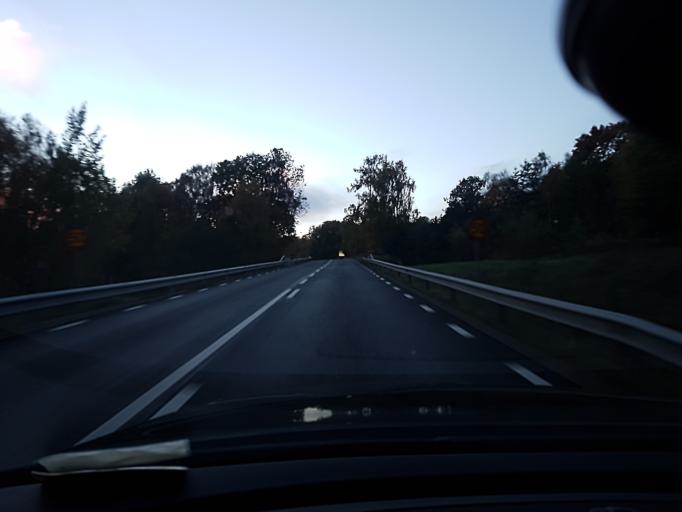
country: SE
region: Halland
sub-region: Laholms Kommun
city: Veinge
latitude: 56.7205
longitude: 13.1350
